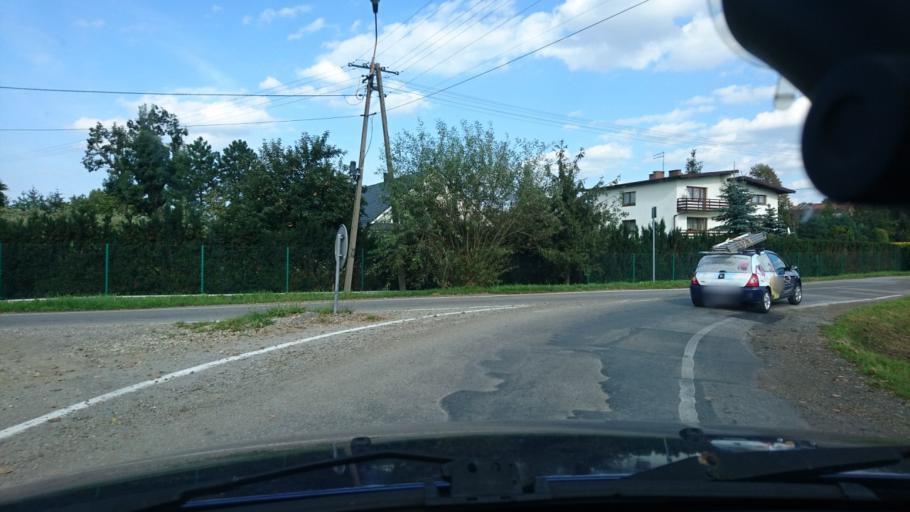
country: PL
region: Silesian Voivodeship
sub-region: Powiat bielski
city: Bronow
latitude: 49.8537
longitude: 18.9438
